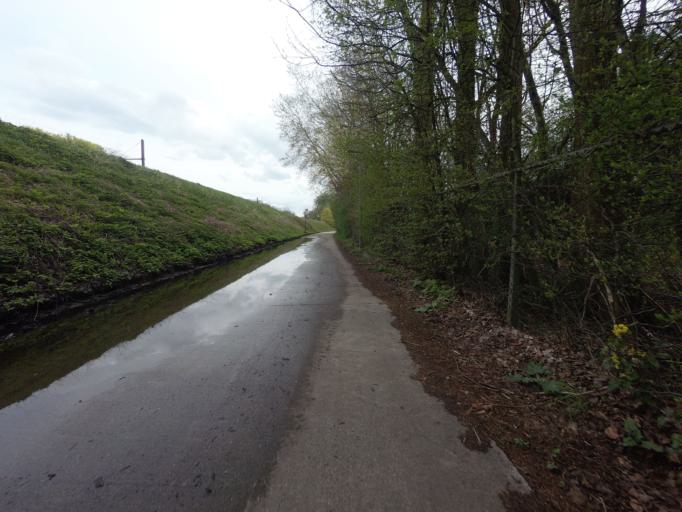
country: BE
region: Flanders
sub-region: Provincie Antwerpen
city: Mortsel
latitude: 51.1851
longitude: 4.4545
